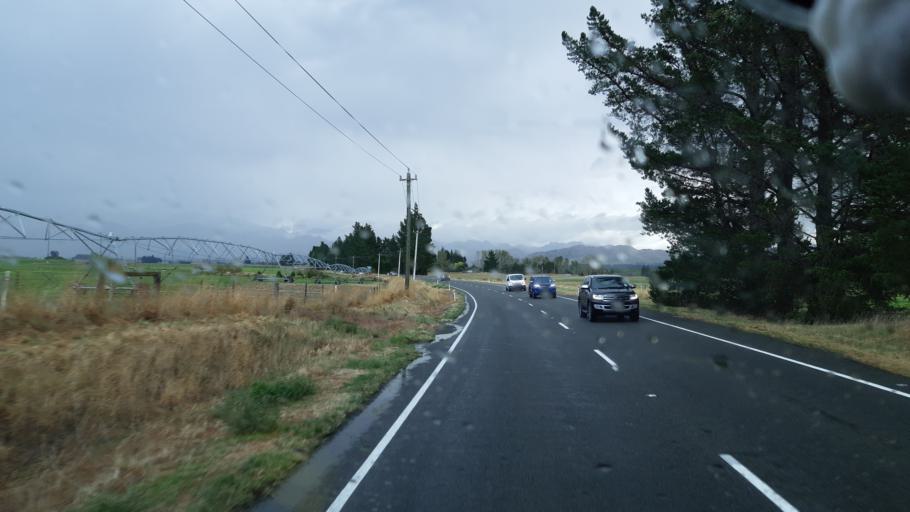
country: NZ
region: Canterbury
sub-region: Hurunui District
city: Amberley
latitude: -42.7137
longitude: 172.8621
